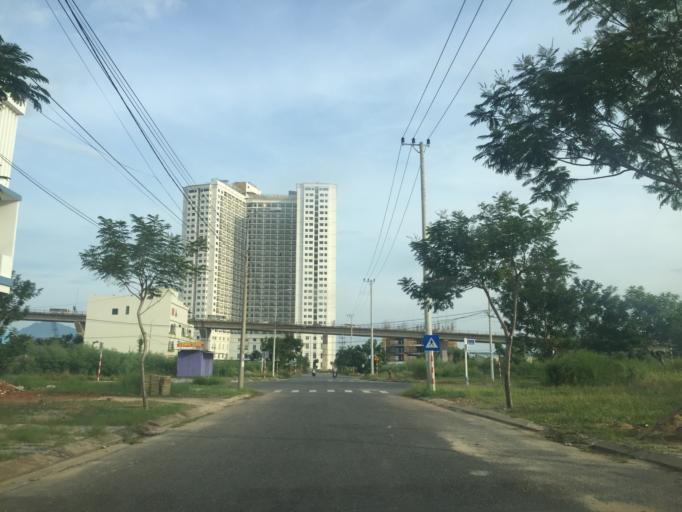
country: VN
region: Da Nang
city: Da Nang
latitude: 16.0955
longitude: 108.2263
